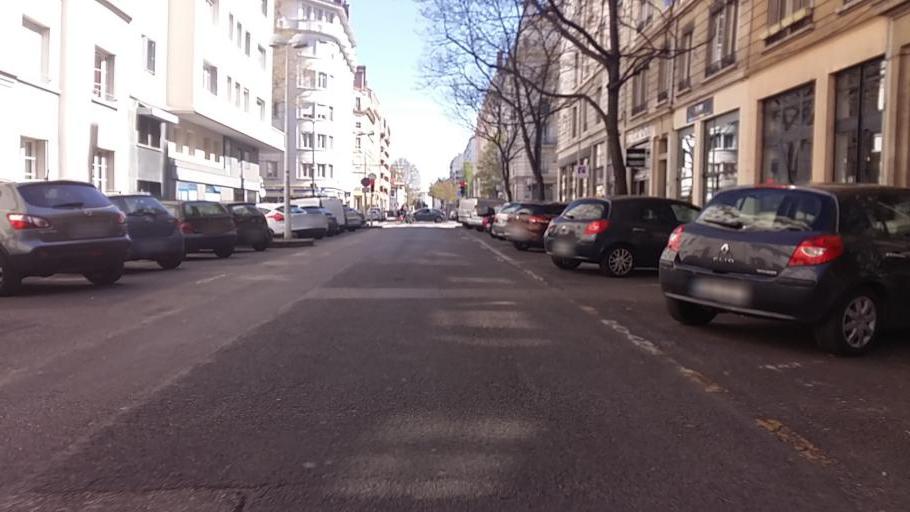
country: FR
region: Rhone-Alpes
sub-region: Departement du Rhone
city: Lyon
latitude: 45.7476
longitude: 4.8423
